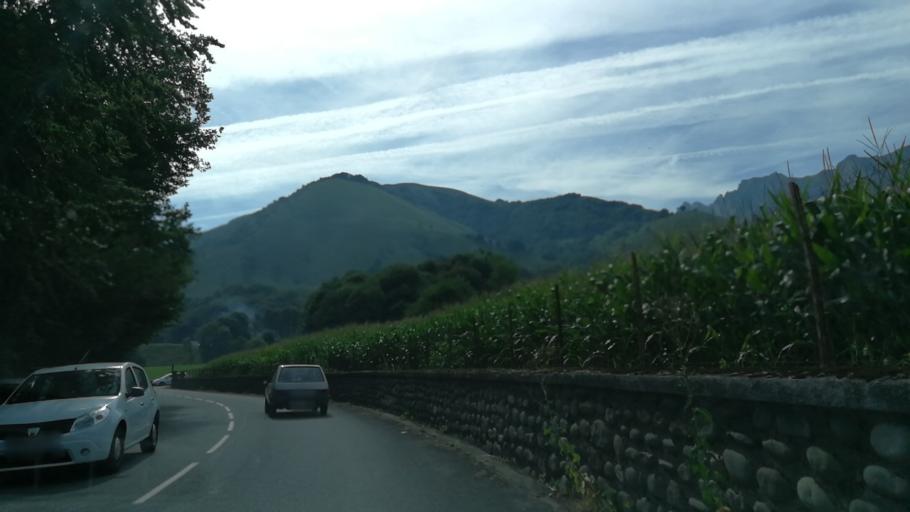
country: FR
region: Aquitaine
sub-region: Departement des Pyrenees-Atlantiques
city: Arette
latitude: 42.9968
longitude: -0.6010
